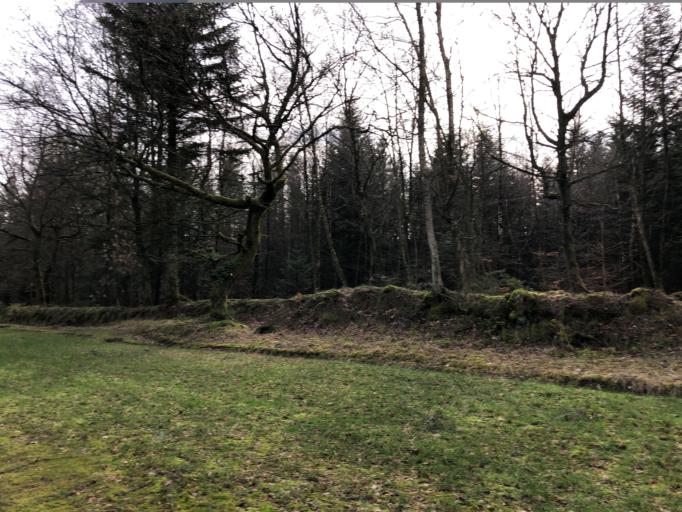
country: DK
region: Central Jutland
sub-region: Holstebro Kommune
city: Ulfborg
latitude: 56.2623
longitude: 8.3863
